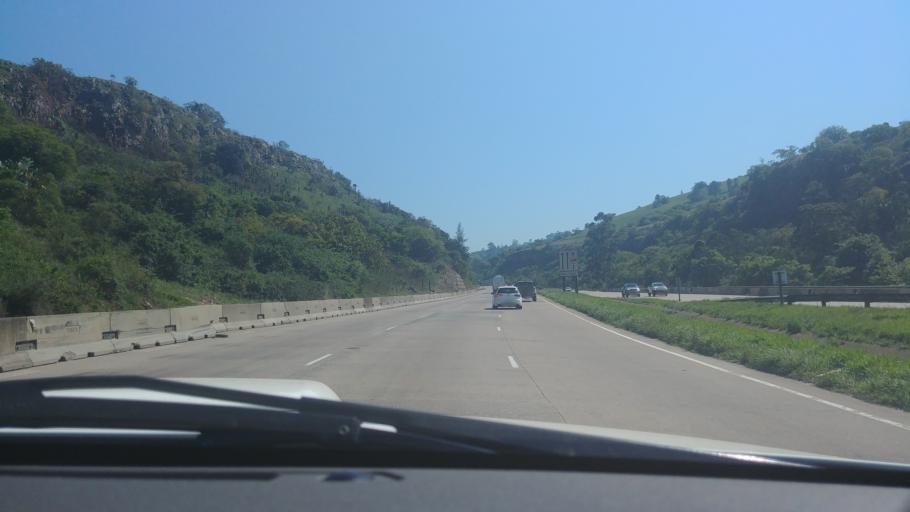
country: ZA
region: KwaZulu-Natal
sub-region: eThekwini Metropolitan Municipality
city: Mpumalanga
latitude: -29.7554
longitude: 30.6648
